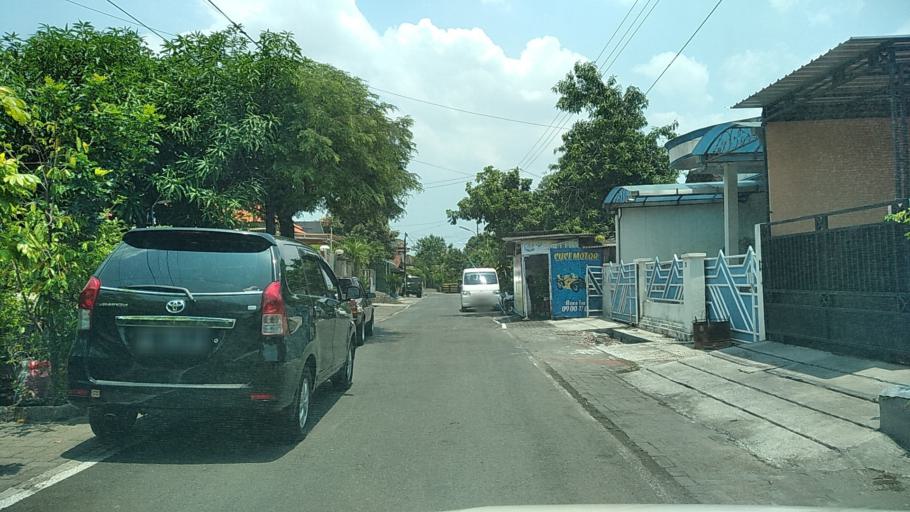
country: ID
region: Central Java
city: Semarang
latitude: -7.0061
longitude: 110.4408
